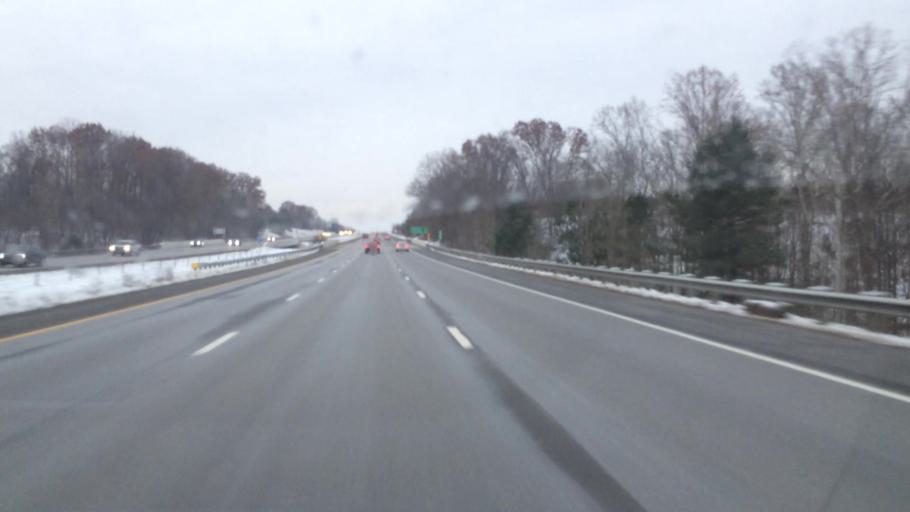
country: US
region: Ohio
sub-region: Medina County
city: Brunswick
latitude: 41.1813
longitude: -81.7885
